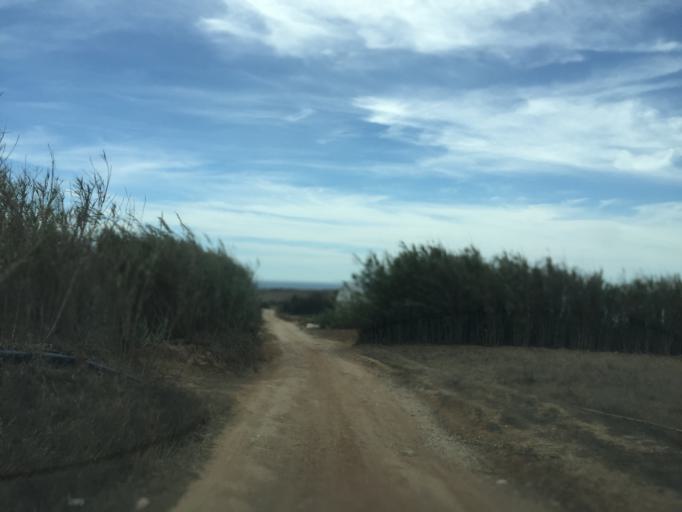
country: PT
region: Lisbon
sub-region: Lourinha
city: Lourinha
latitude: 39.1910
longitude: -9.3449
